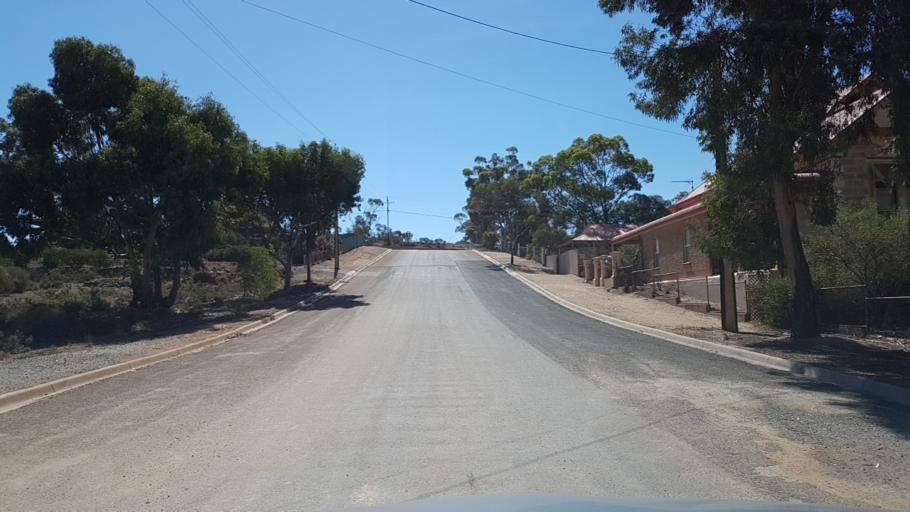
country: AU
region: South Australia
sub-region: Peterborough
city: Peterborough
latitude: -32.9713
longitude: 138.8346
